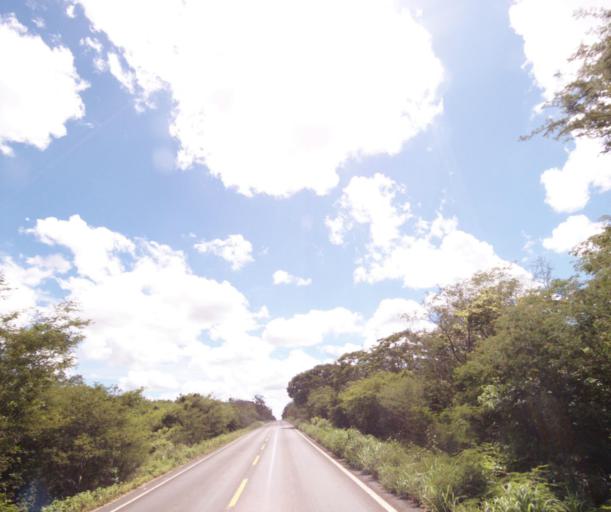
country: BR
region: Bahia
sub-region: Sao Felix Do Coribe
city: Santa Maria da Vitoria
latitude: -13.3553
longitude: -43.9612
